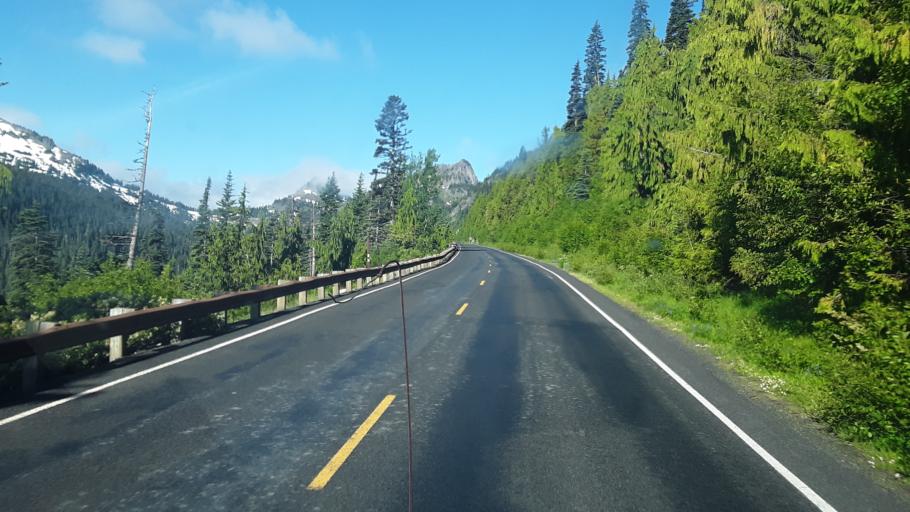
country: US
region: Washington
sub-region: King County
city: Enumclaw
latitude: 46.8929
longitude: -121.4848
